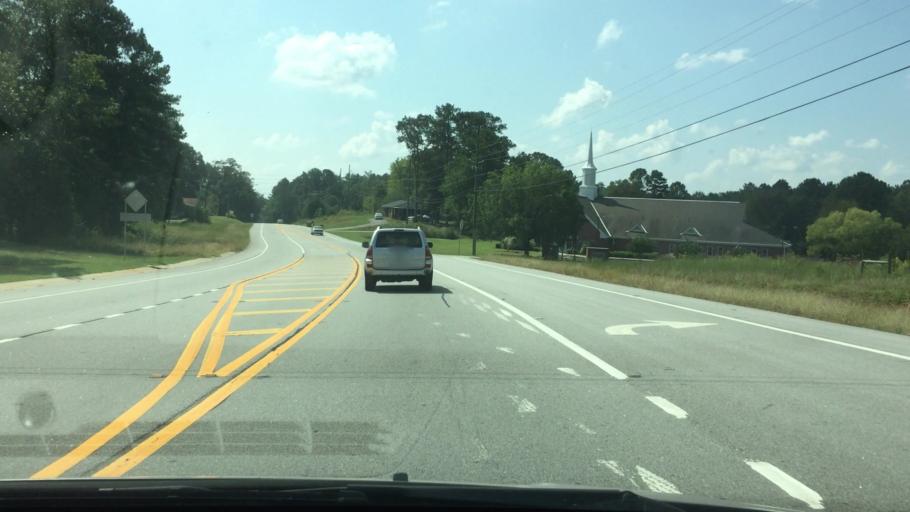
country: US
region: Georgia
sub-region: Henry County
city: Stockbridge
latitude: 33.5429
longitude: -84.1389
